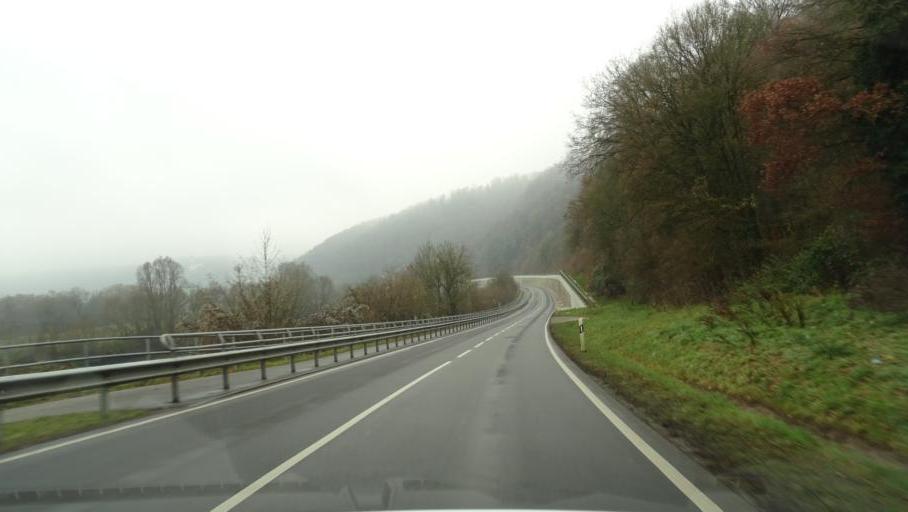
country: DE
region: Baden-Wuerttemberg
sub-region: Karlsruhe Region
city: Hassmersheim
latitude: 49.2963
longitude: 9.1317
